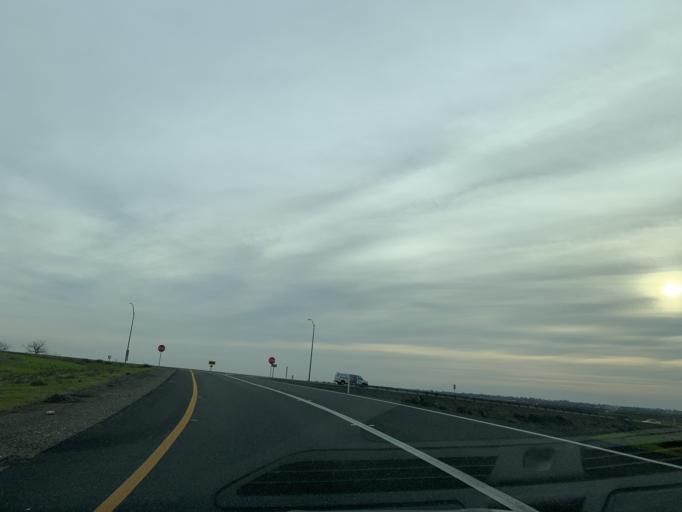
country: US
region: California
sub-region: Sacramento County
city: Elverta
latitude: 38.6864
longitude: -121.5418
